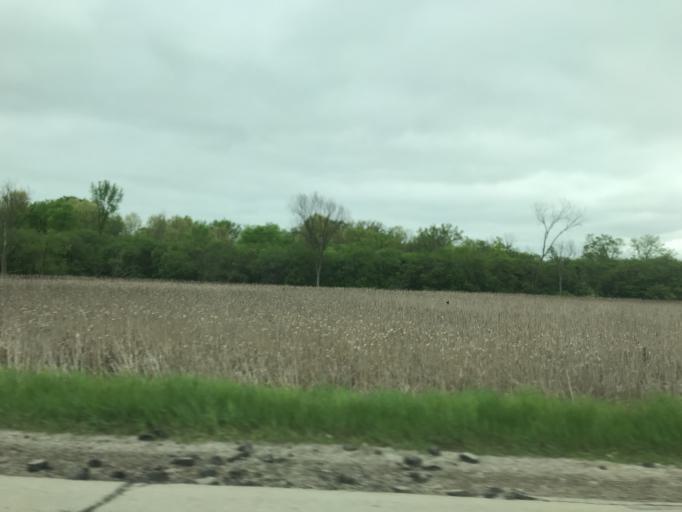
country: US
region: Michigan
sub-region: Washtenaw County
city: Ann Arbor
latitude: 42.2352
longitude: -83.7059
